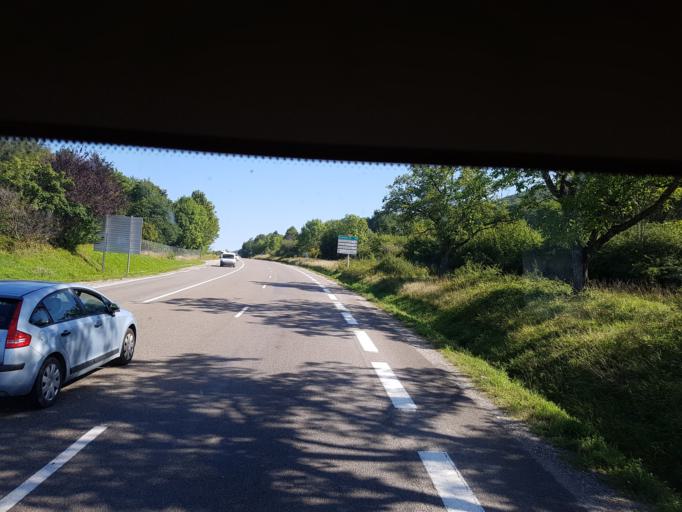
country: FR
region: Franche-Comte
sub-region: Departement du Jura
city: Perrigny
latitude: 46.6767
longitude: 5.5854
